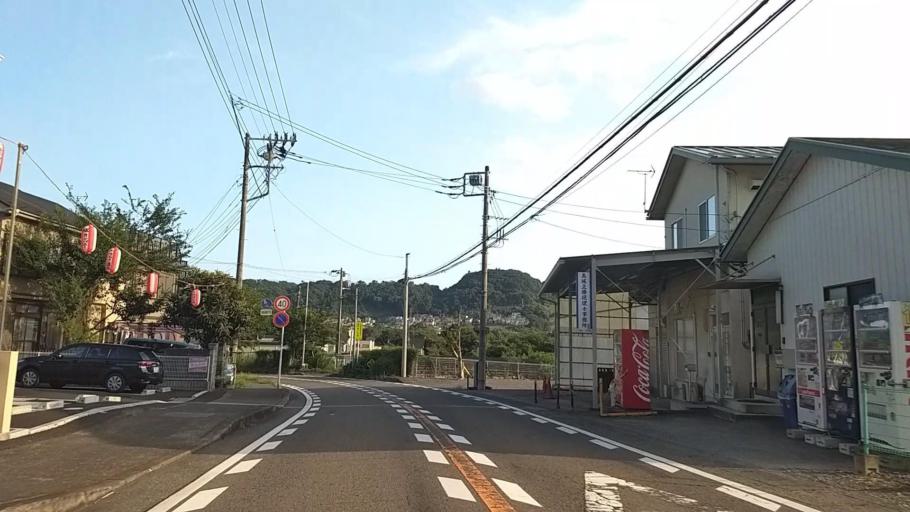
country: JP
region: Tokyo
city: Hachioji
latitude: 35.5917
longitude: 139.2630
